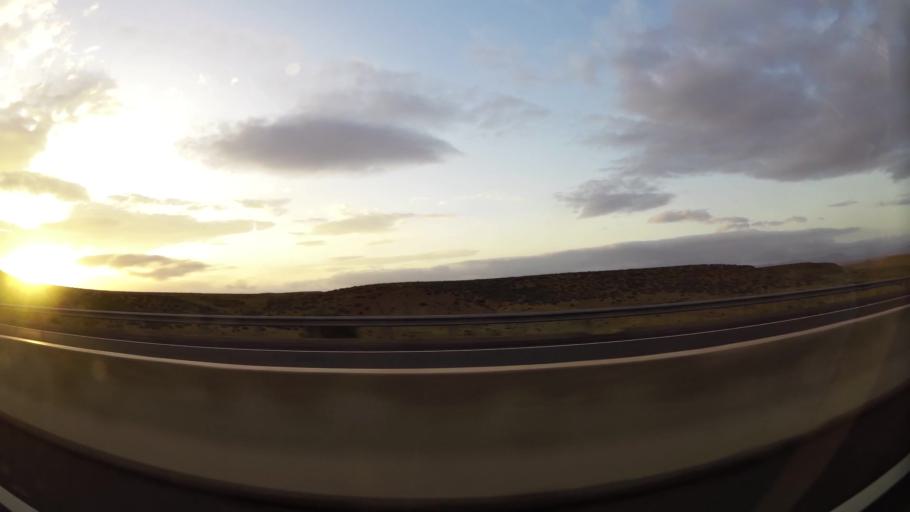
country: MA
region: Oriental
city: Taourirt
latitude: 34.4997
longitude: -2.9604
